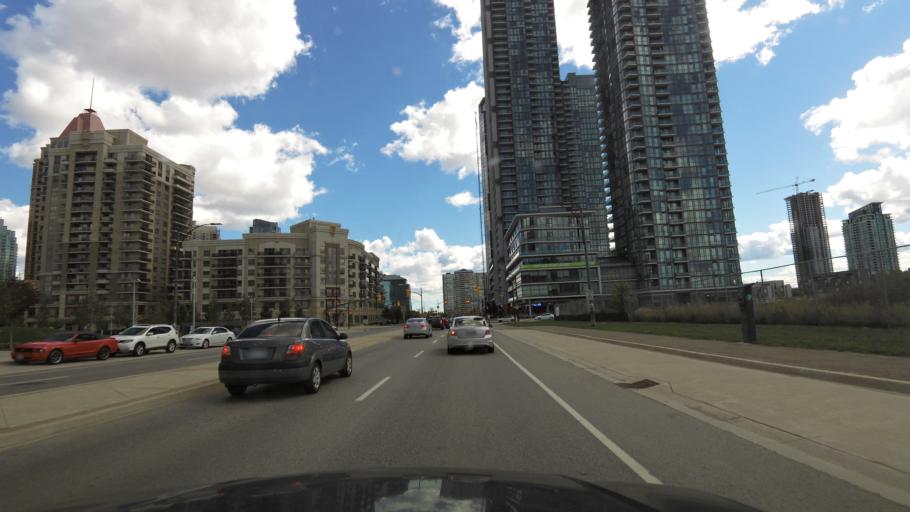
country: CA
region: Ontario
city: Mississauga
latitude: 43.5877
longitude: -79.6486
